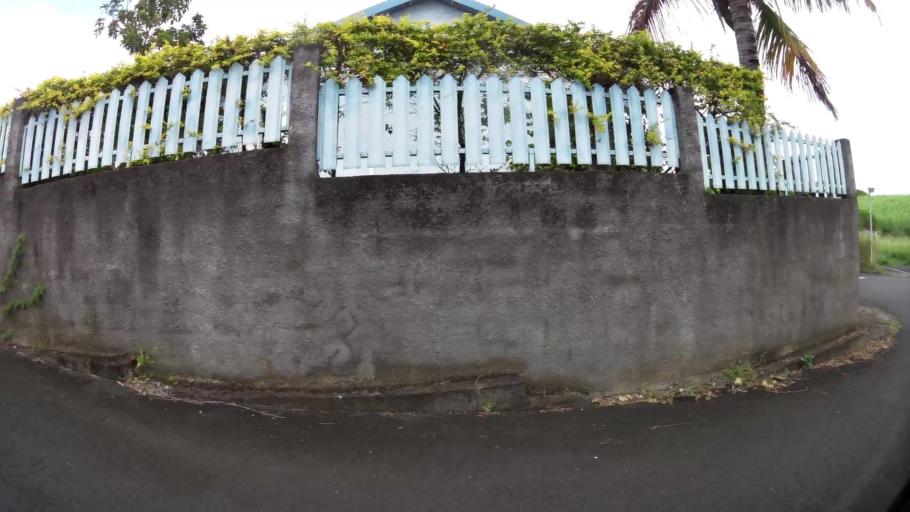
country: RE
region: Reunion
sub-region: Reunion
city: Sainte-Marie
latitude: -20.8963
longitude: 55.5627
